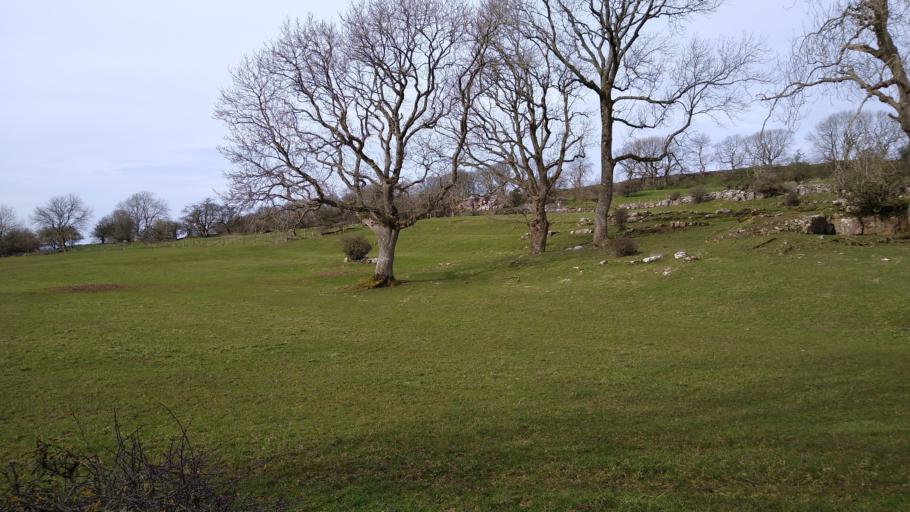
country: GB
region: England
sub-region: Cumbria
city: Cockermouth
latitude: 54.6974
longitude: -3.3690
